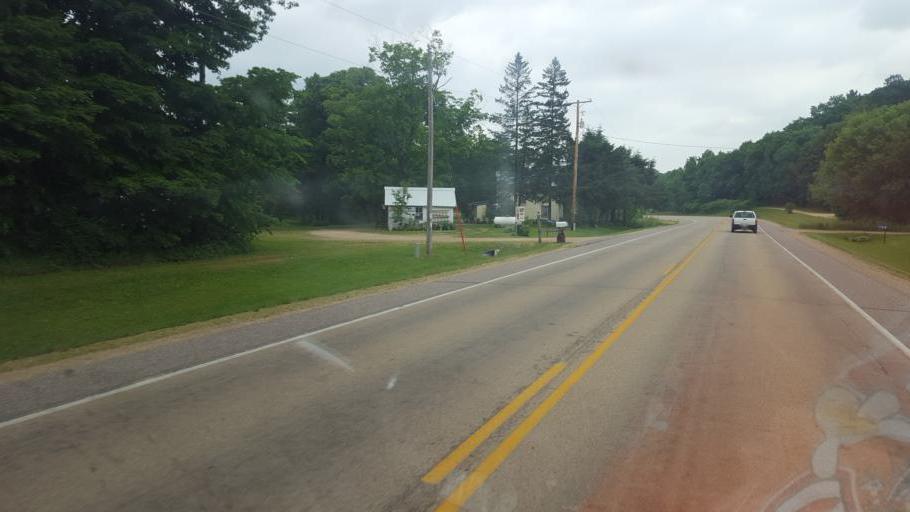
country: US
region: Wisconsin
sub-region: Juneau County
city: Elroy
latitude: 43.6403
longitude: -90.1845
